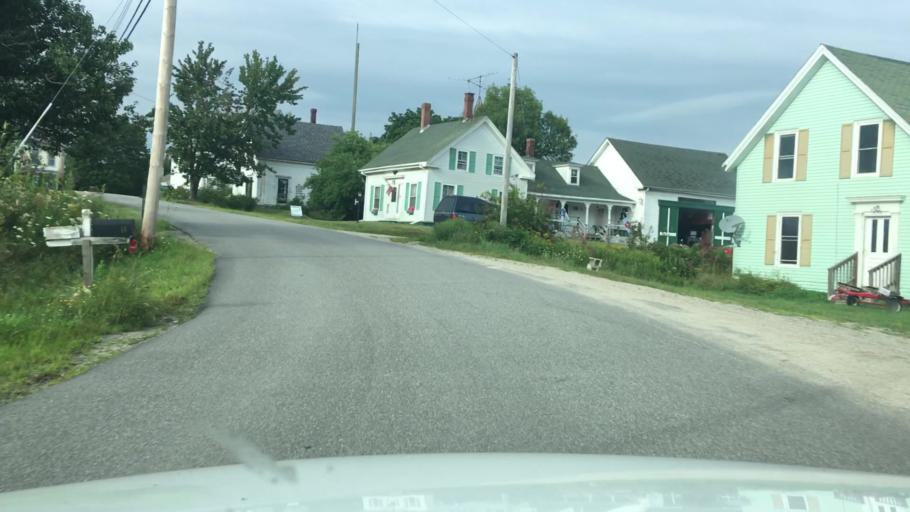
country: US
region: Maine
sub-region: Washington County
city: Addison
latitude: 44.6182
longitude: -67.8111
